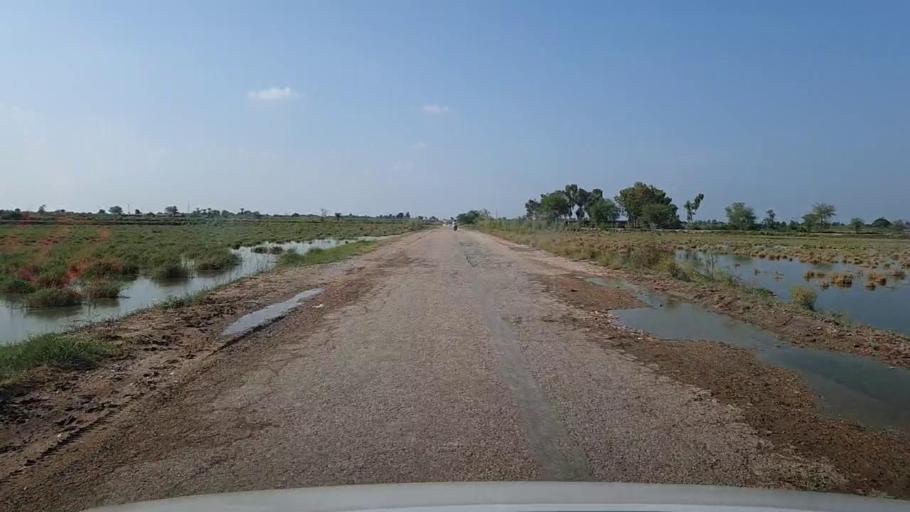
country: PK
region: Sindh
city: Kandiaro
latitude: 27.0631
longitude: 68.3157
